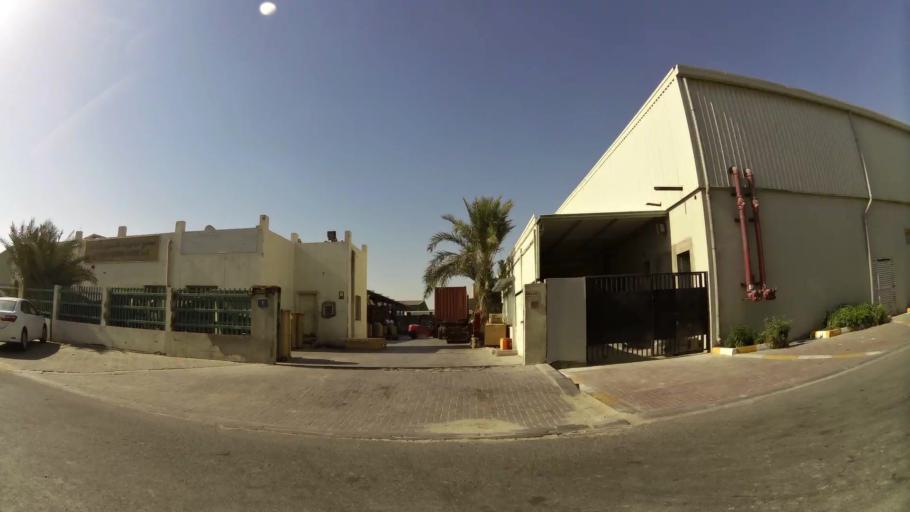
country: AE
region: Dubai
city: Dubai
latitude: 24.9940
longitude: 55.1001
